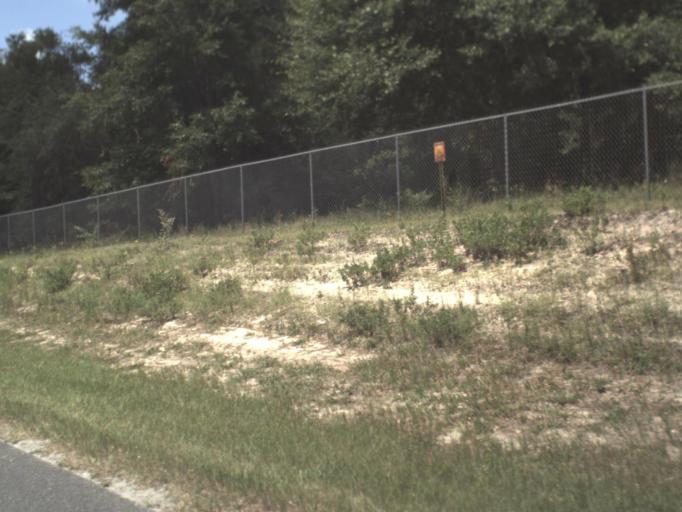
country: US
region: Florida
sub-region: Gilchrist County
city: Trenton
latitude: 29.7714
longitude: -82.8666
